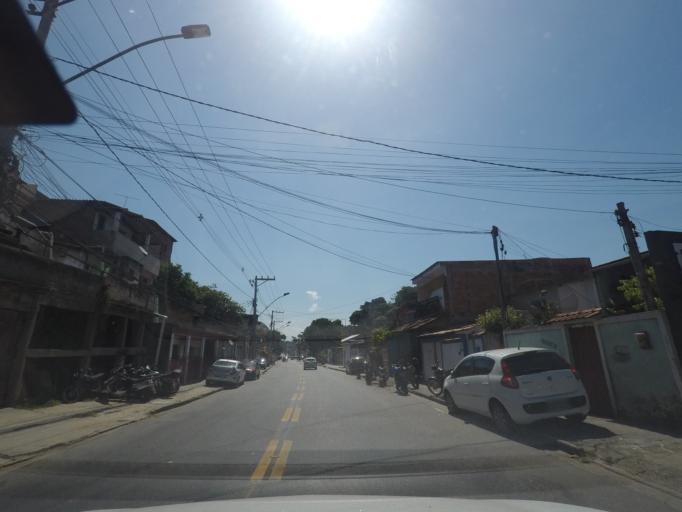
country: BR
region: Rio de Janeiro
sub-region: Niteroi
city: Niteroi
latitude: -22.9105
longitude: -43.0523
